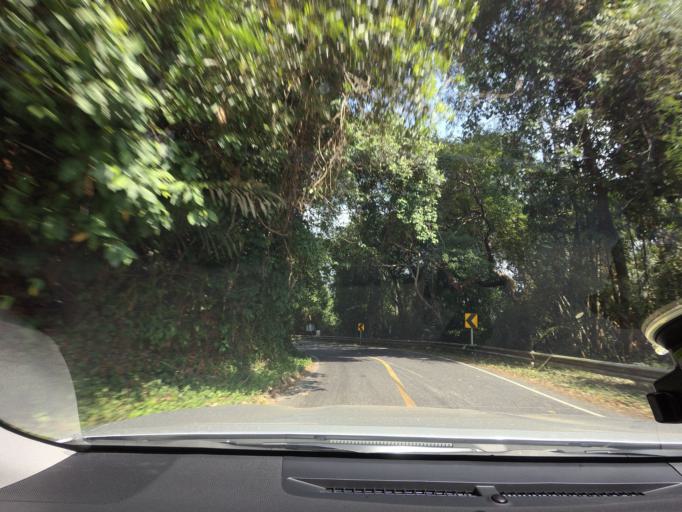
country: TH
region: Phangnga
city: Thap Put
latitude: 8.5357
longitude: 98.5596
